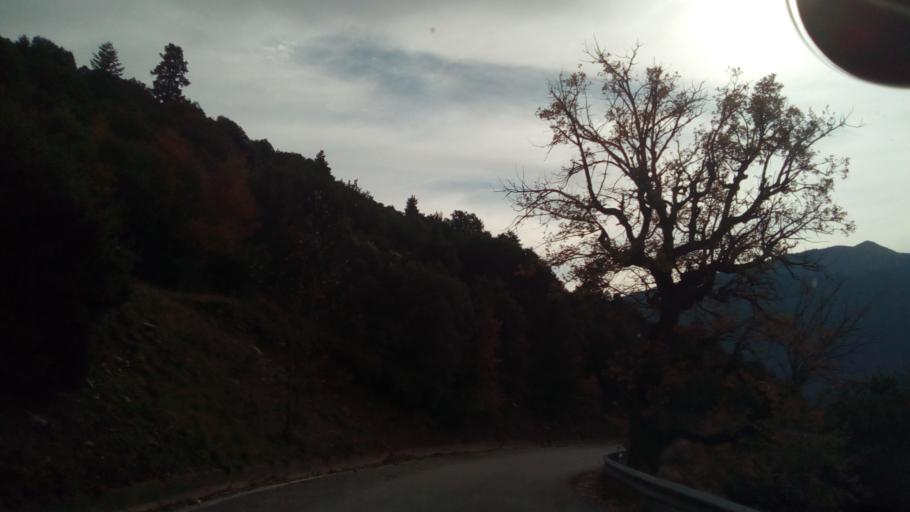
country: GR
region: West Greece
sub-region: Nomos Aitolias kai Akarnanias
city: Thermo
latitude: 38.6776
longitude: 21.8818
